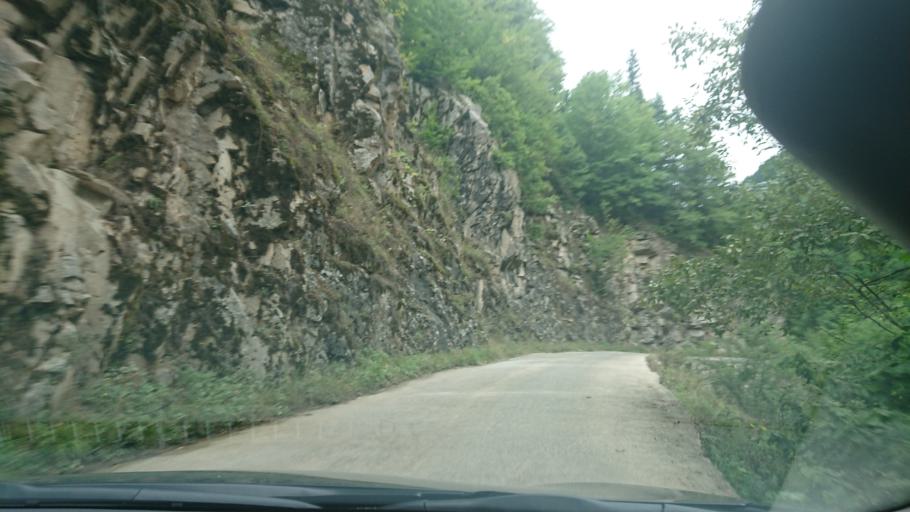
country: TR
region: Gumushane
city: Kurtun
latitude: 40.6794
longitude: 39.0485
